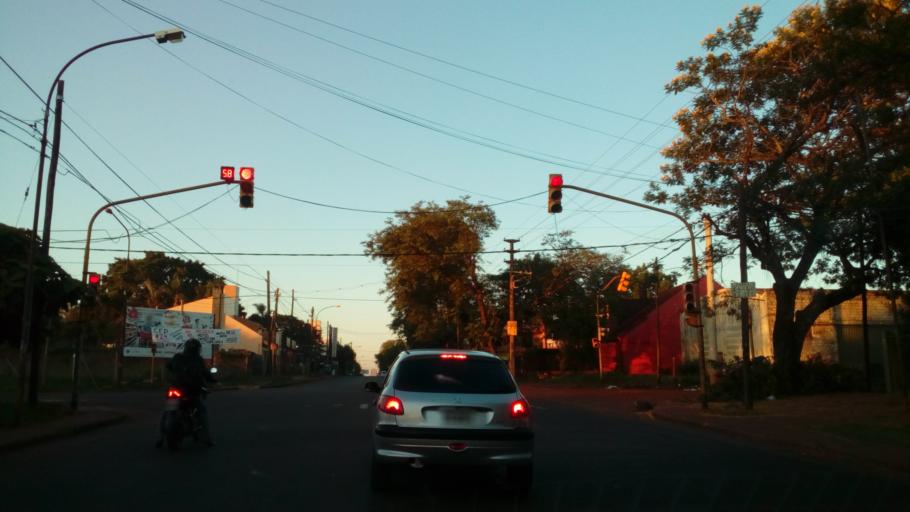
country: AR
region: Misiones
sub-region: Departamento de Capital
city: Posadas
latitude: -27.4020
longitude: -55.8986
